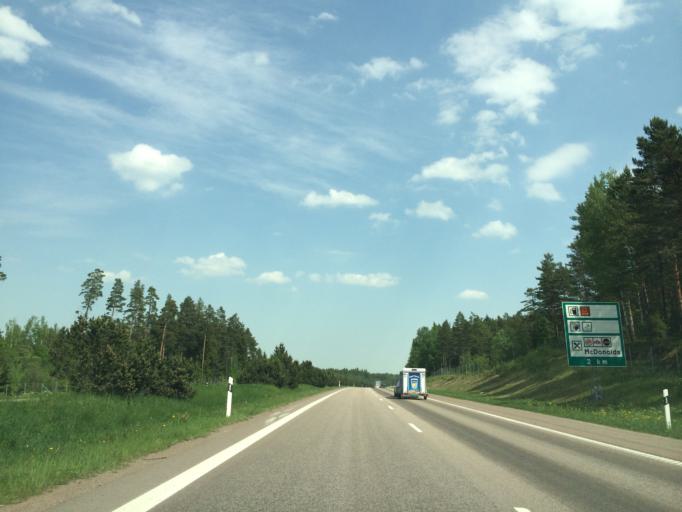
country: SE
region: OEstergoetland
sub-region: Mjolby Kommun
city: Mjolby
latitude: 58.3181
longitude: 15.0534
